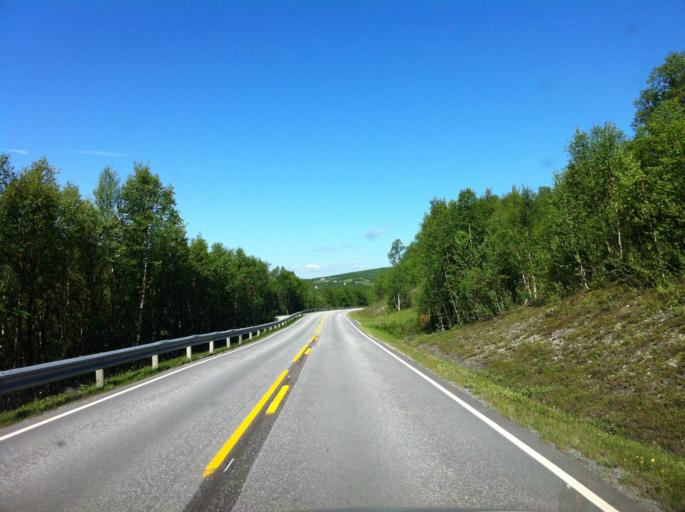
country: NO
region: Sor-Trondelag
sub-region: Roros
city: Roros
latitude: 62.5905
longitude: 11.7887
